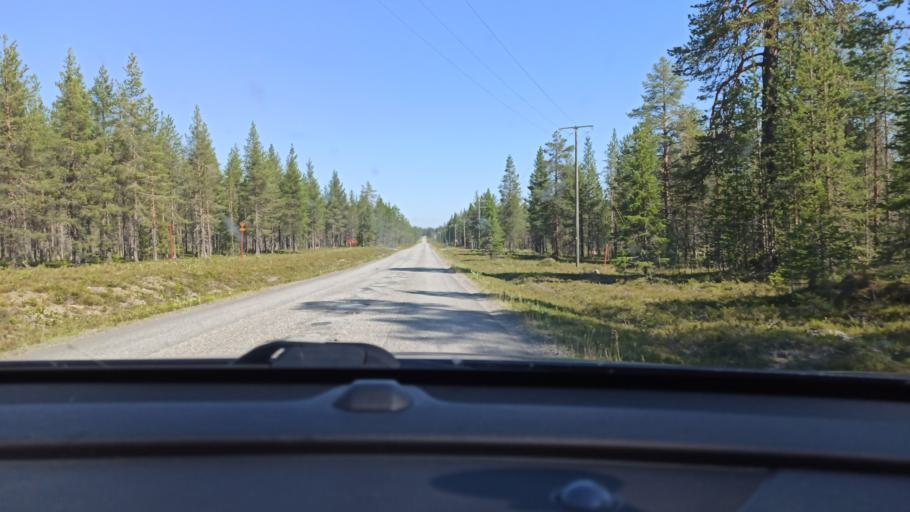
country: FI
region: Lapland
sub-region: Tunturi-Lappi
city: Kolari
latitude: 67.6458
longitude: 24.1600
